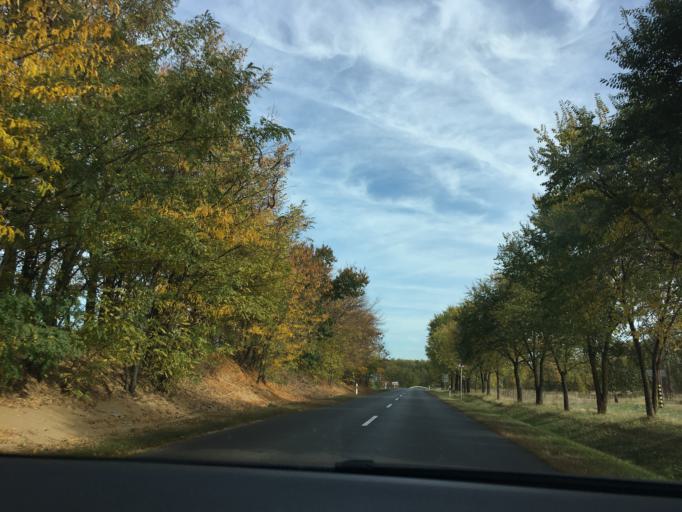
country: HU
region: Szabolcs-Szatmar-Bereg
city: Kisleta
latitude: 47.8529
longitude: 22.0218
